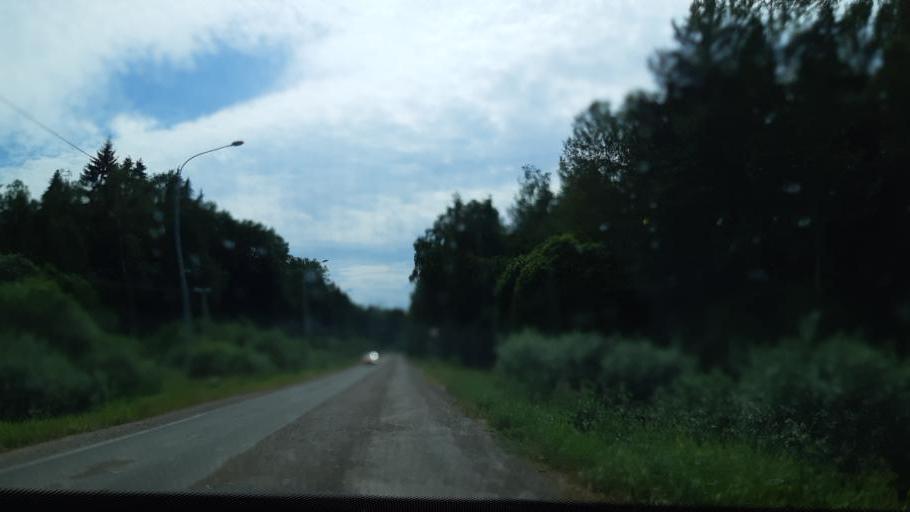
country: RU
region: Moskovskaya
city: Vereya
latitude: 55.2385
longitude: 36.0388
